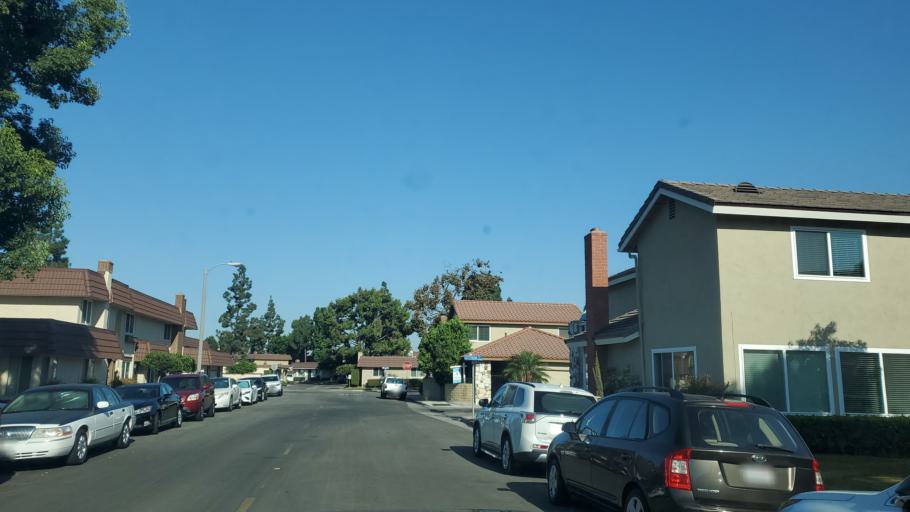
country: US
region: California
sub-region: Orange County
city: Stanton
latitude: 33.7973
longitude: -118.0174
